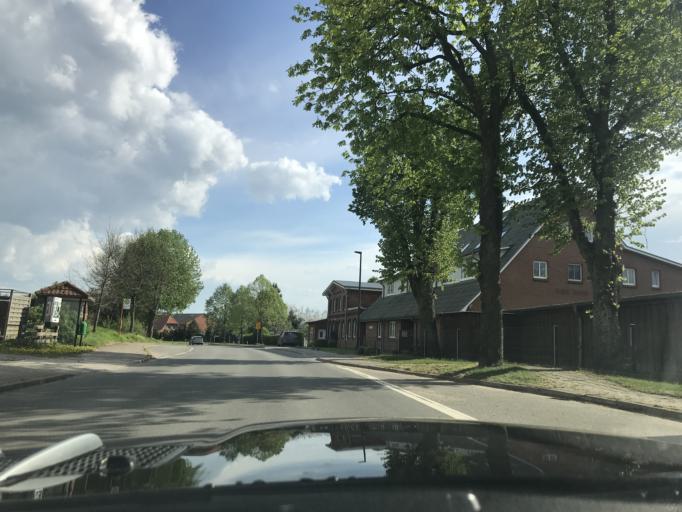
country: DE
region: Schleswig-Holstein
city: Woltersdorf
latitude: 53.5779
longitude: 10.6396
